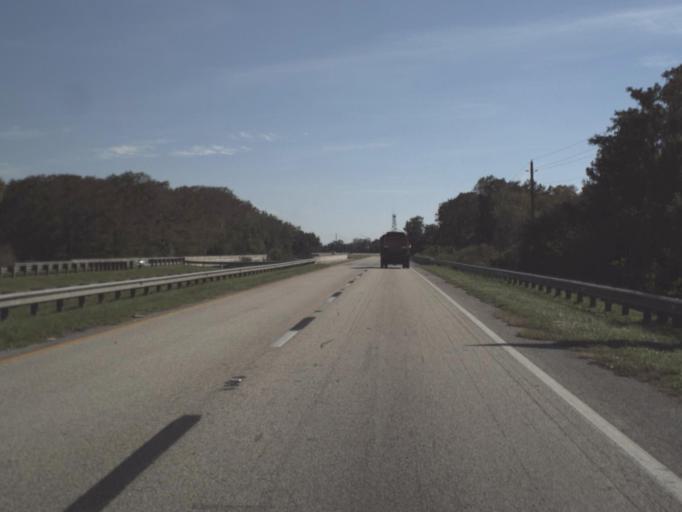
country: US
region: Florida
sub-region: Hendry County
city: Port LaBelle
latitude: 26.9323
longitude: -81.3152
